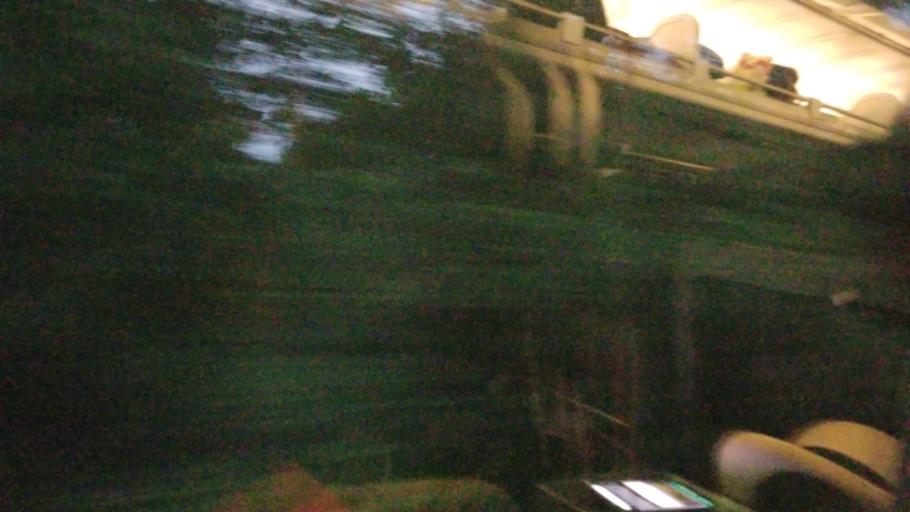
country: US
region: Virginia
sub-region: Albemarle County
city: Hollymead
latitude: 38.1446
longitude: -78.3765
